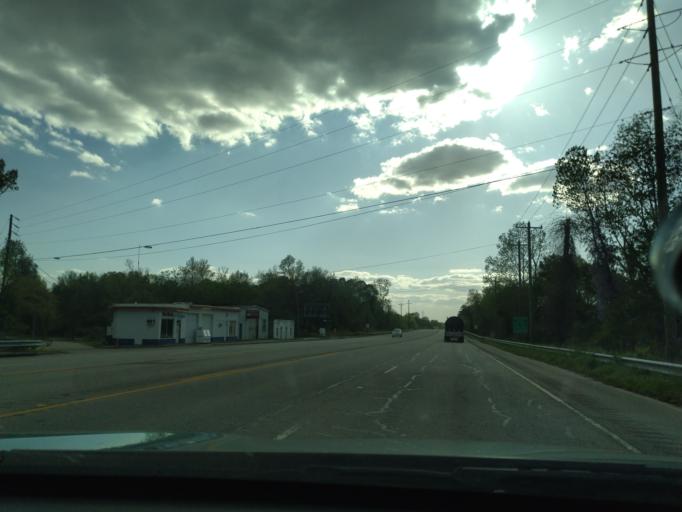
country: US
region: South Carolina
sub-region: Williamsburg County
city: Kingstree
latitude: 33.6622
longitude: -79.8370
